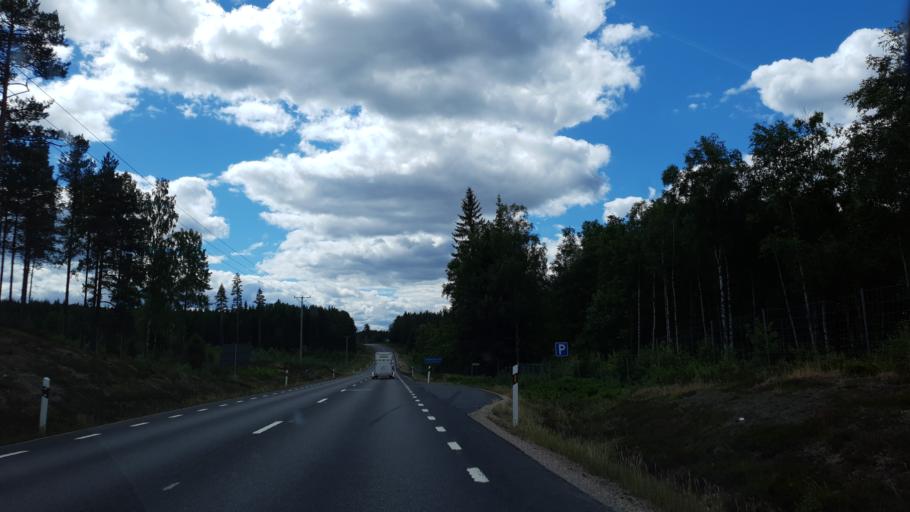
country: SE
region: Kronoberg
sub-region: Vaxjo Kommun
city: Braas
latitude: 57.1876
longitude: 15.1565
